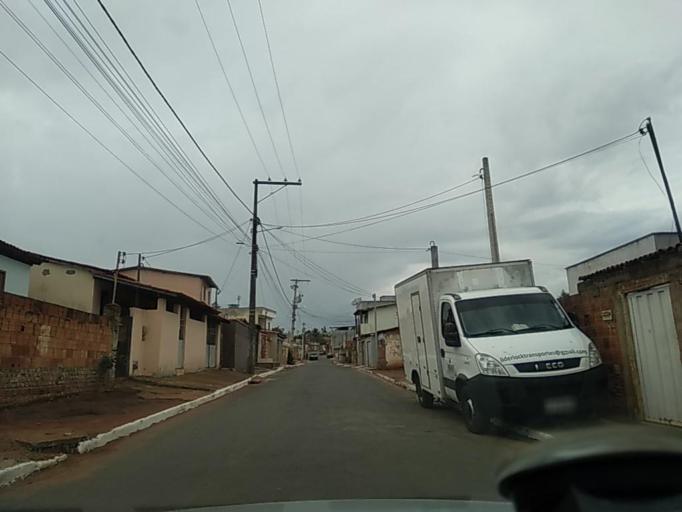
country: BR
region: Bahia
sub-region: Caetite
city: Caetite
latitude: -14.0556
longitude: -42.4807
